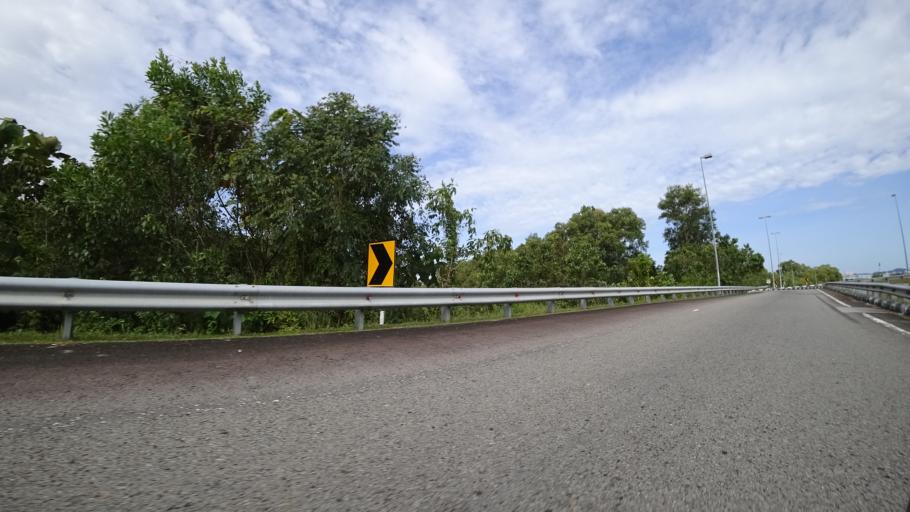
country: BN
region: Brunei and Muara
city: Bandar Seri Begawan
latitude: 4.9214
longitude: 114.9120
